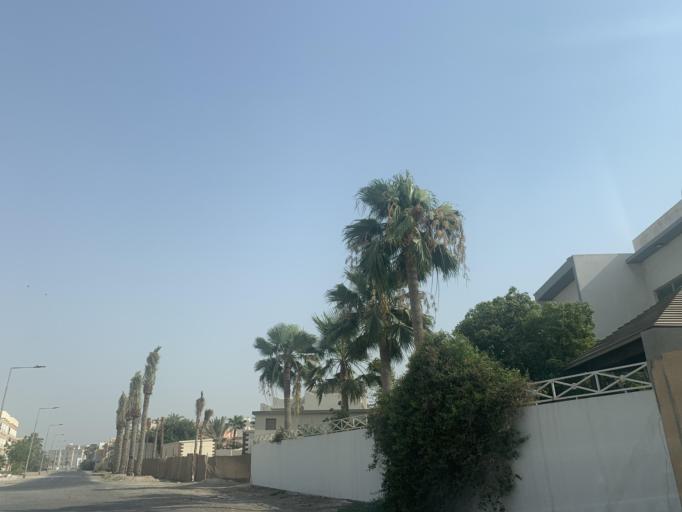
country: BH
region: Manama
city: Jidd Hafs
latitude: 26.2062
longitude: 50.4948
